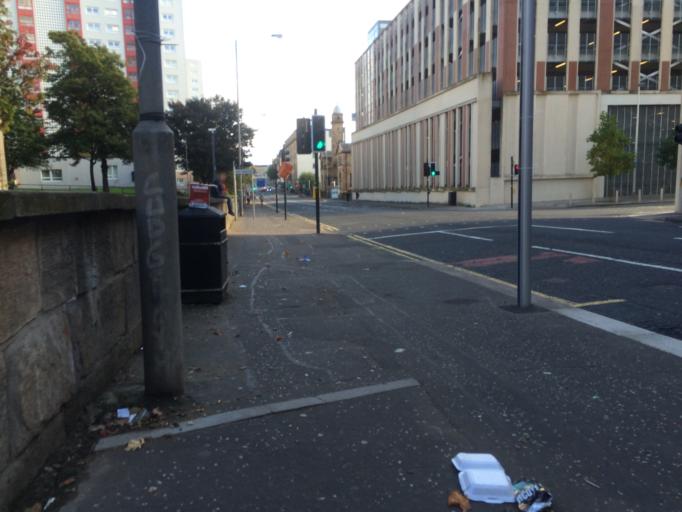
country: GB
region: Scotland
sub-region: Glasgow City
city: Glasgow
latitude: 55.8600
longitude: -4.2377
